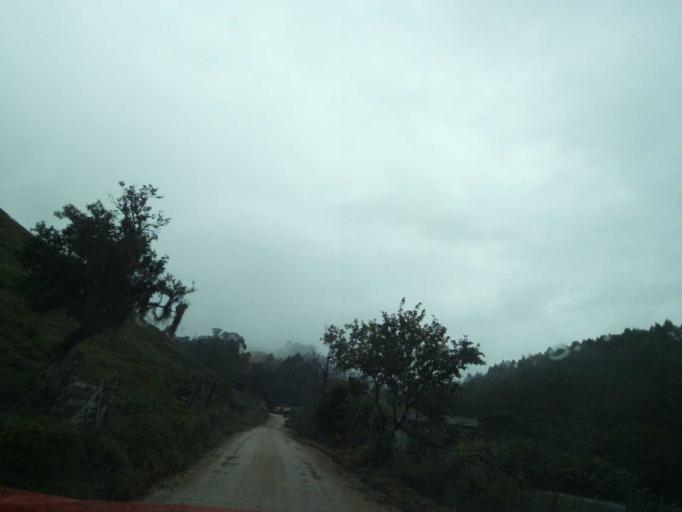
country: BR
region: Santa Catarina
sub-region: Anitapolis
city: Anitapolis
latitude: -27.8969
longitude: -49.1939
